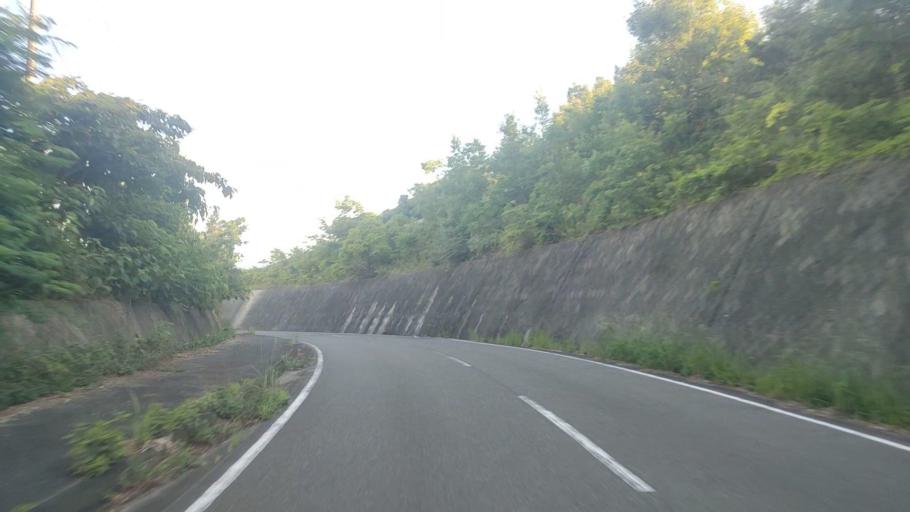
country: JP
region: Wakayama
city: Tanabe
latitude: 33.7734
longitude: 135.3056
